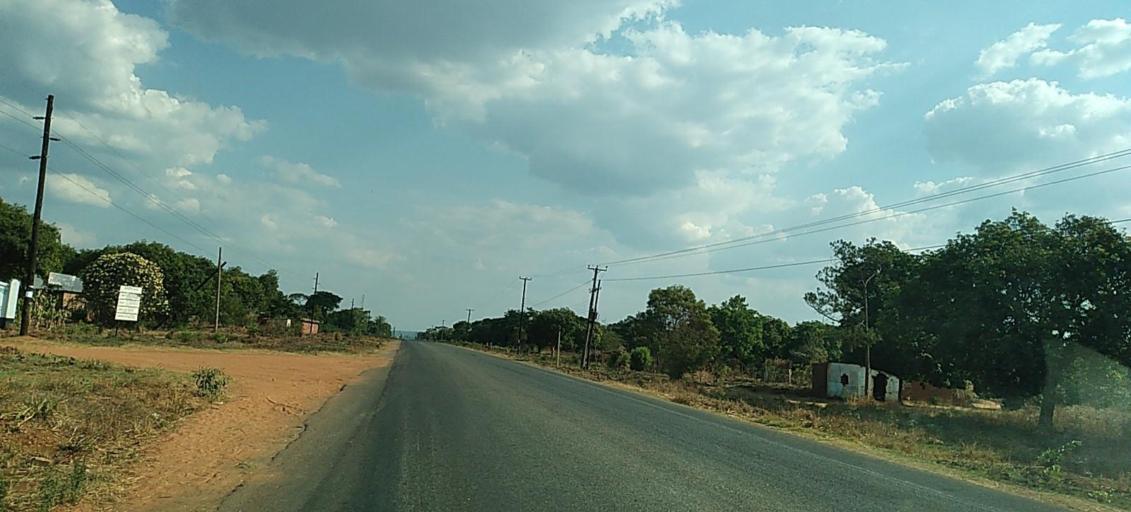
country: ZM
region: Copperbelt
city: Luanshya
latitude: -13.3149
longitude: 28.4140
